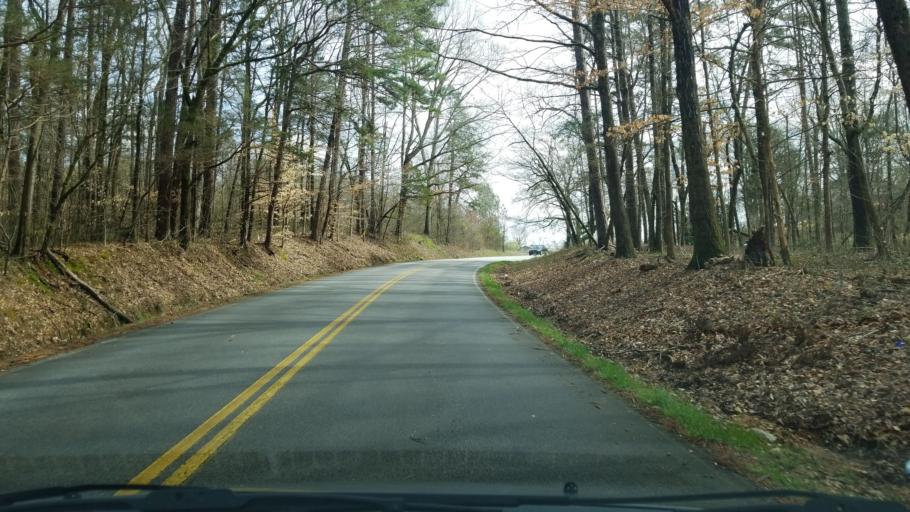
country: US
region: Tennessee
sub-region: Hamilton County
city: Harrison
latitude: 35.1342
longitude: -85.0759
